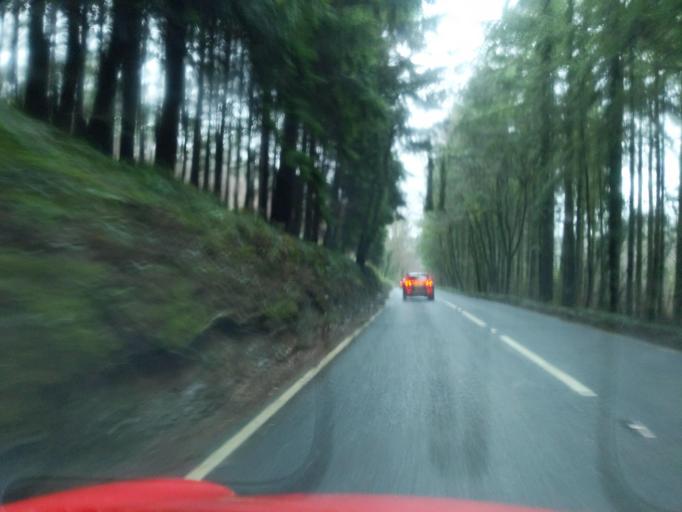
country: GB
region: England
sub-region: Cornwall
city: South Hill
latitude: 50.5648
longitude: -4.3340
